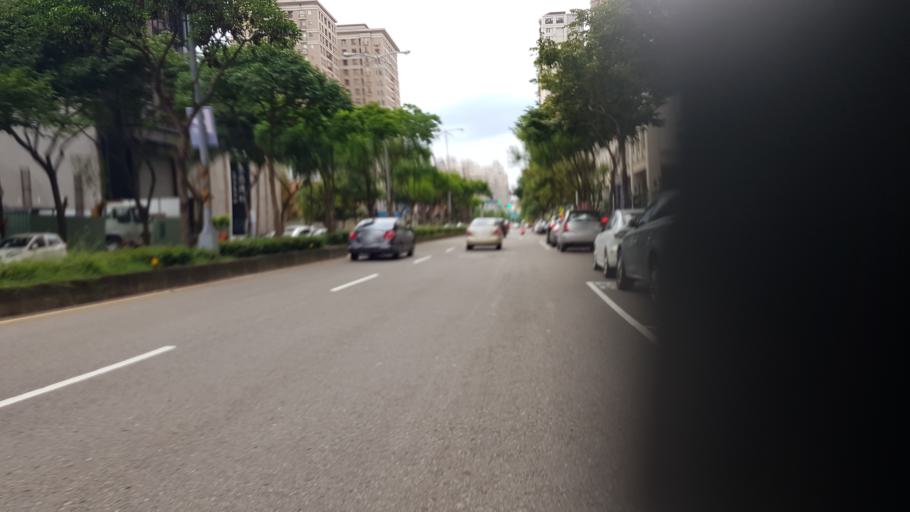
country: TW
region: Taiwan
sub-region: Hsinchu
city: Zhubei
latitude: 24.8070
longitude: 121.0367
